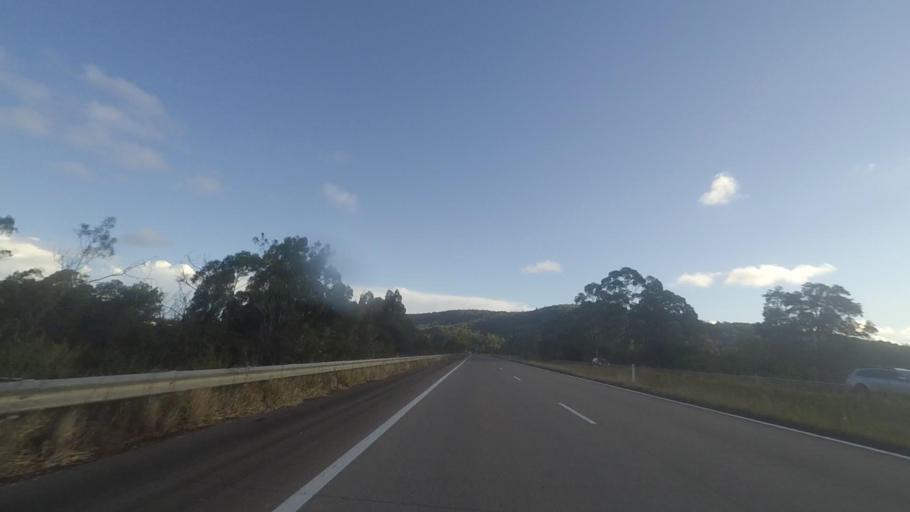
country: AU
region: New South Wales
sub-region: Great Lakes
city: Nabiac
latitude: -32.2671
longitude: 152.3283
